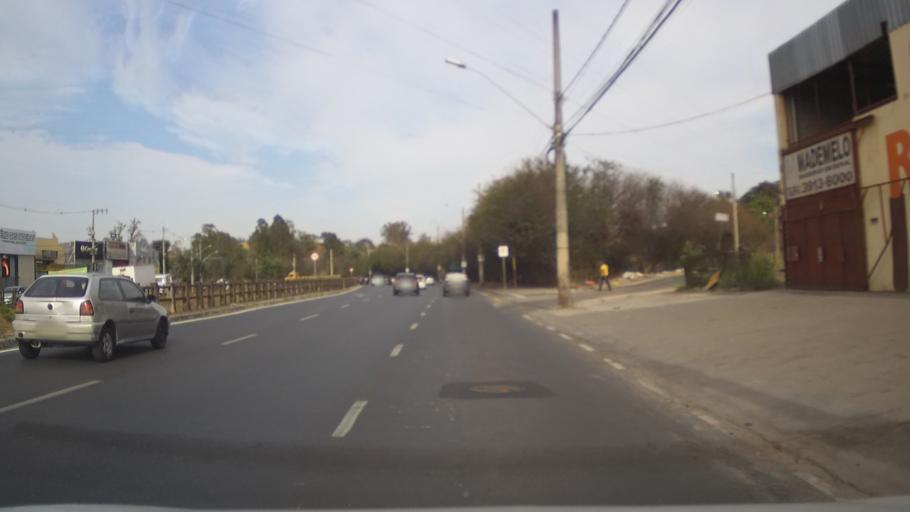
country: BR
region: Minas Gerais
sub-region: Contagem
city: Contagem
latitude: -19.8730
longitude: -44.0224
